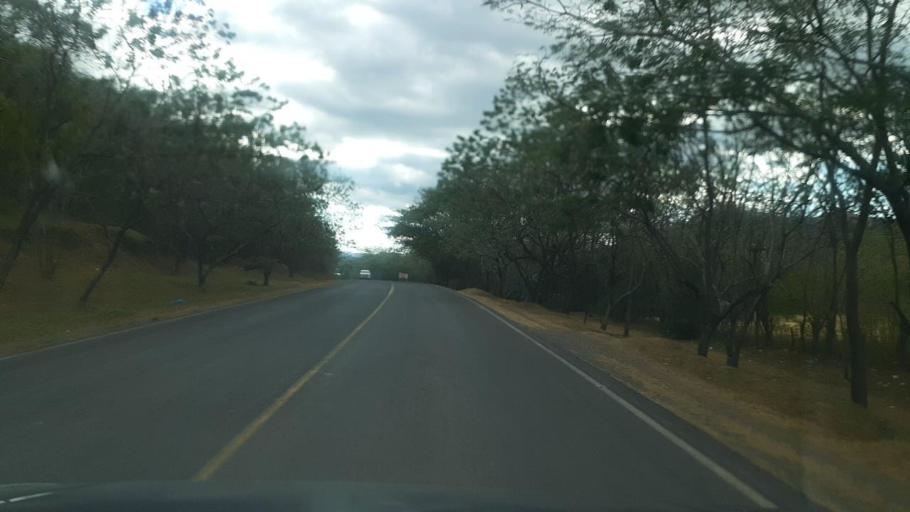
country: NI
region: Madriz
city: Somoto
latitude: 13.5028
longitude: -86.5702
